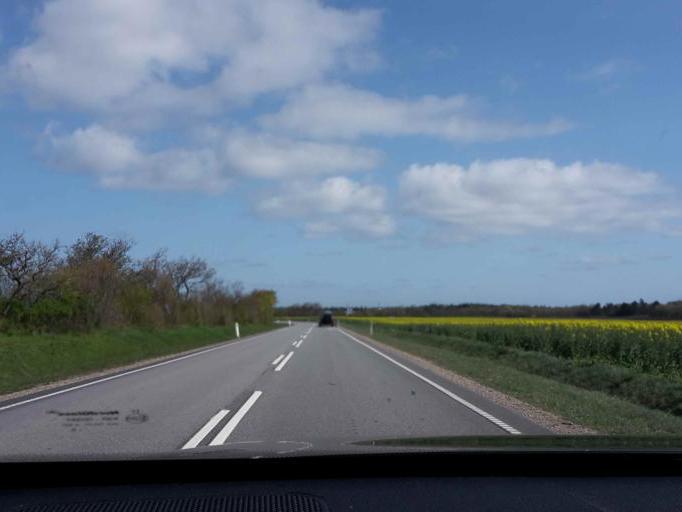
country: DK
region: South Denmark
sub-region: Billund Kommune
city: Grindsted
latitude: 55.6518
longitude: 8.9569
